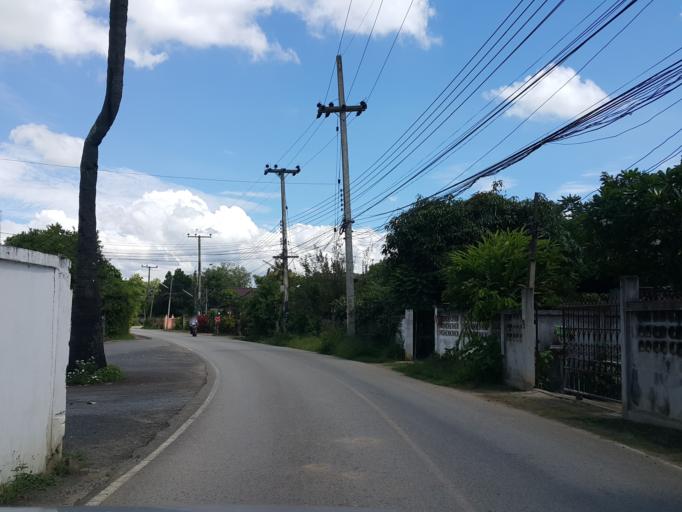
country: TH
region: Chiang Mai
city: San Kamphaeng
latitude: 18.7608
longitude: 99.1204
